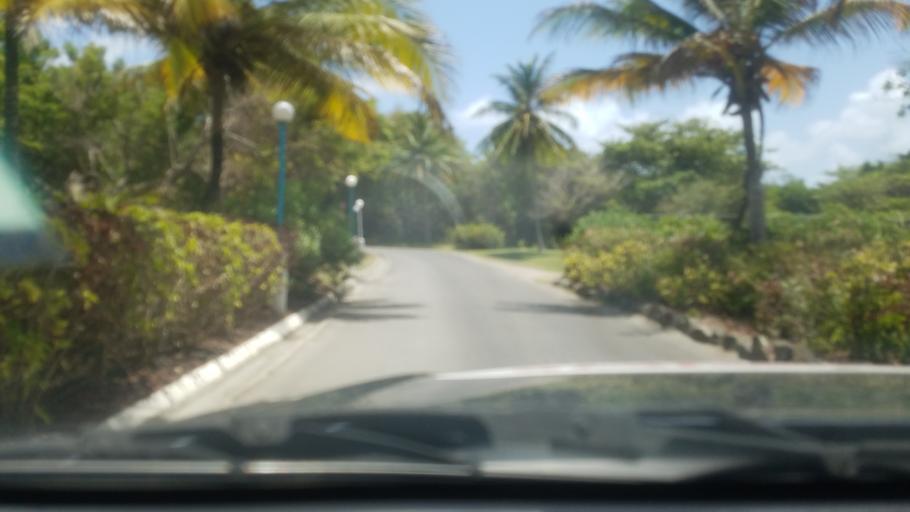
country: LC
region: Vieux-Fort
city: Vieux Fort
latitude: 13.7371
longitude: -60.9406
